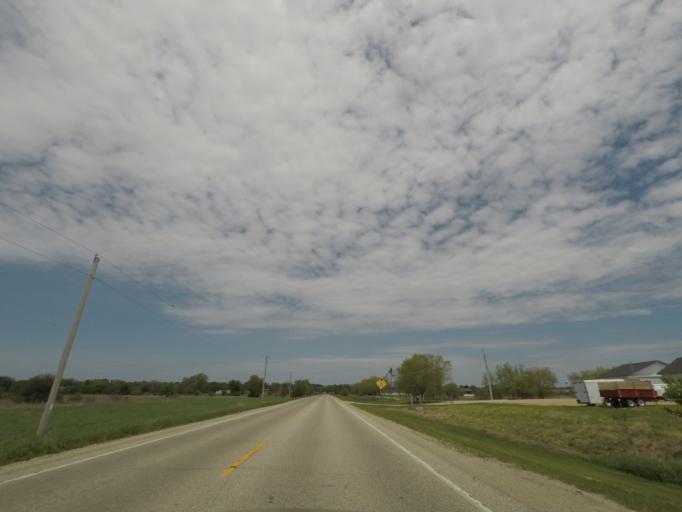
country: US
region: Wisconsin
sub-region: Rock County
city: Evansville
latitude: 42.7659
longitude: -89.2990
